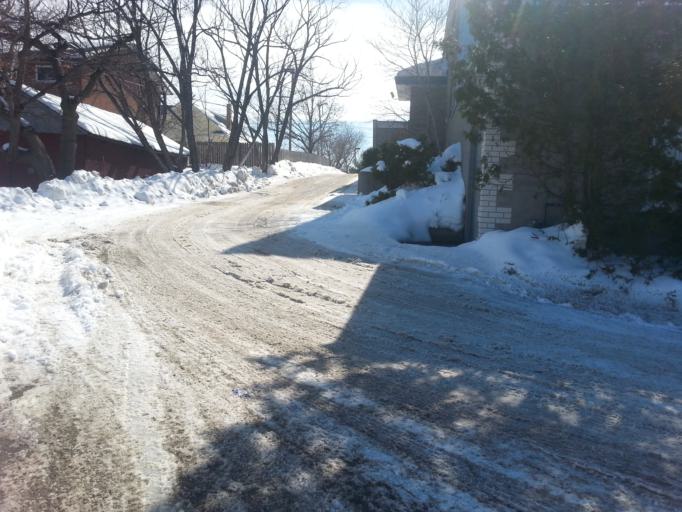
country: CA
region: Ontario
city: Greater Sudbury
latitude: 46.4951
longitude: -81.0078
